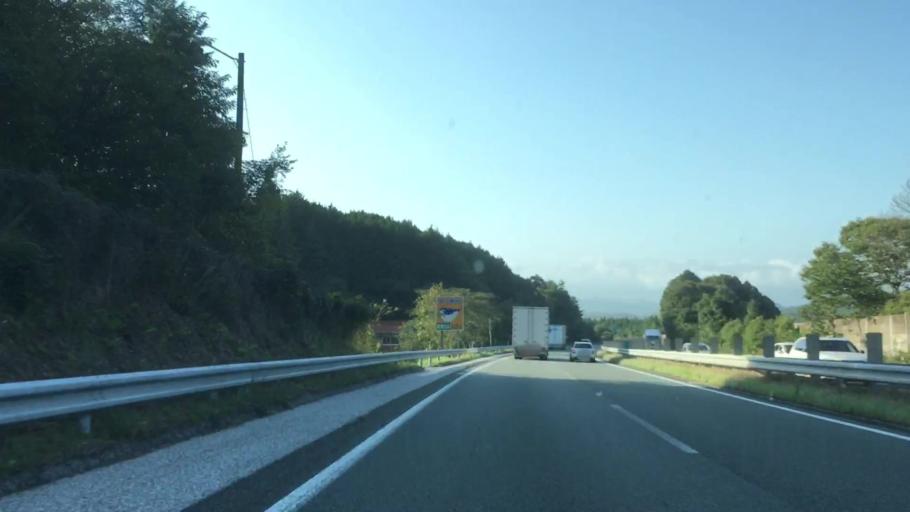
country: JP
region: Yamaguchi
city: Ogori-shimogo
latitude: 34.1474
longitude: 131.3441
